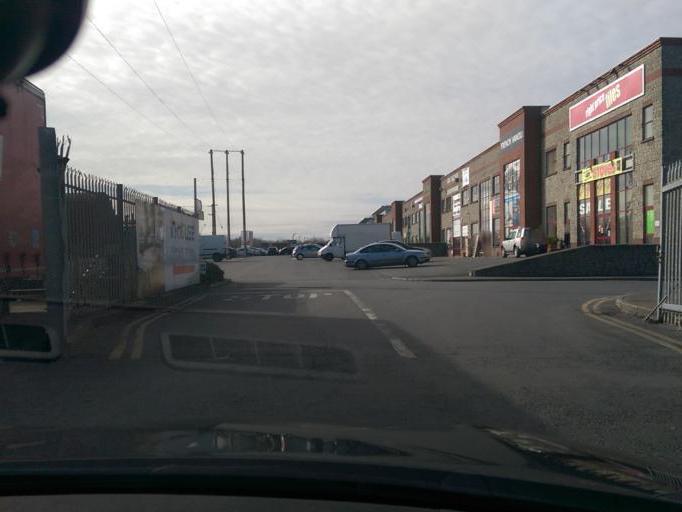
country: IE
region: Connaught
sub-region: County Galway
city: Oranmore
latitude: 53.2773
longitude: -8.9288
